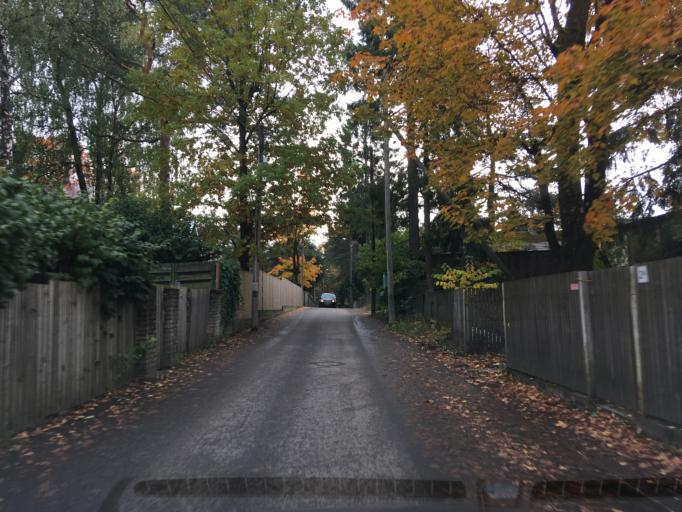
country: EE
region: Harju
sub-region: Tallinna linn
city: Tallinn
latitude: 59.3869
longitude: 24.6968
